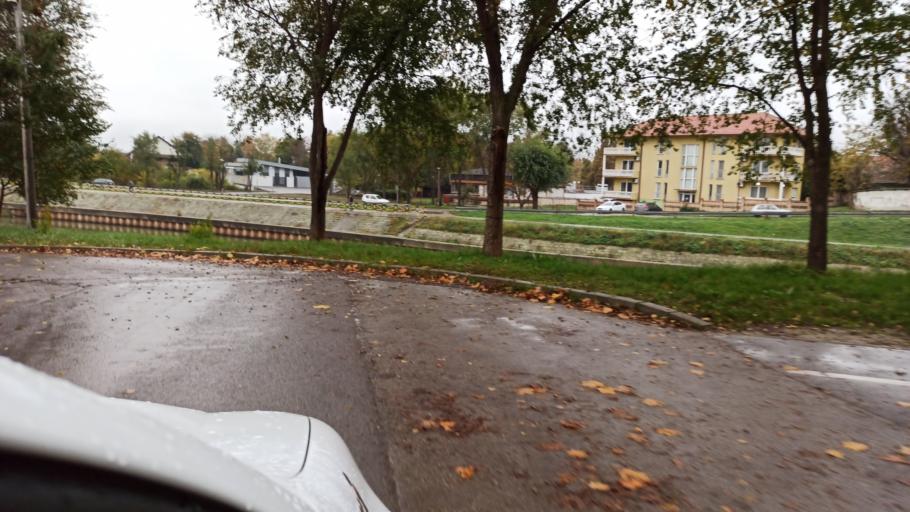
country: RS
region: Autonomna Pokrajina Vojvodina
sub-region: Srednjebanatski Okrug
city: Zrenjanin
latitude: 45.3750
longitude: 20.3929
